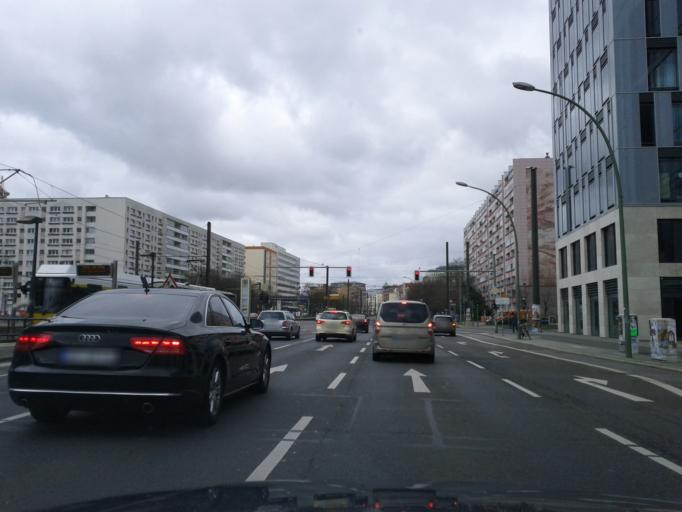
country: DE
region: Berlin
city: Berlin
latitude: 52.5249
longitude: 13.4211
